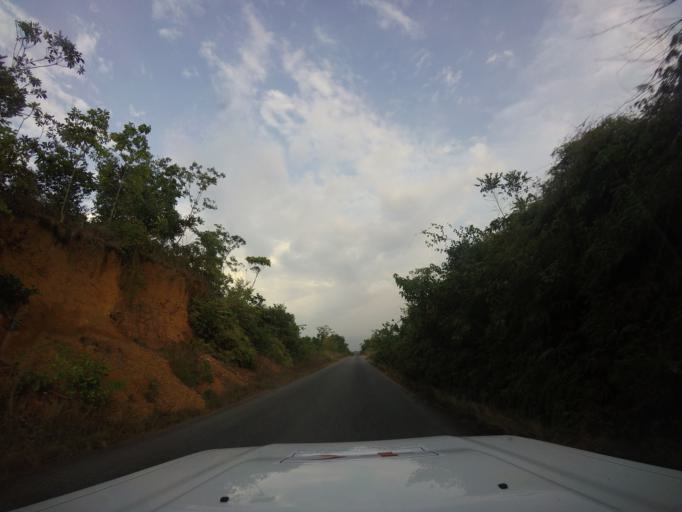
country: LR
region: Bomi
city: Tubmanburg
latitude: 6.7103
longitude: -10.9332
